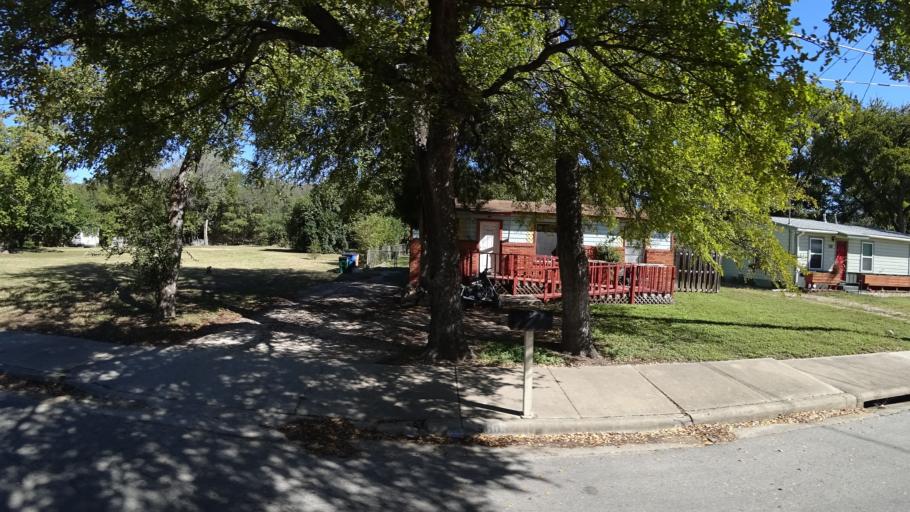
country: US
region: Texas
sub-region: Travis County
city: Austin
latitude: 30.2830
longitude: -97.6774
